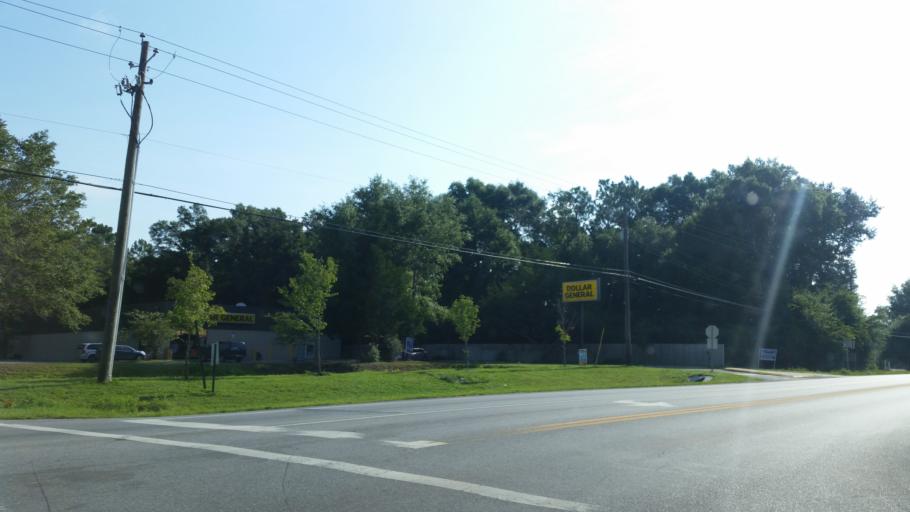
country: US
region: Florida
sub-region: Escambia County
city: Bellview
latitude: 30.4614
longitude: -87.3158
